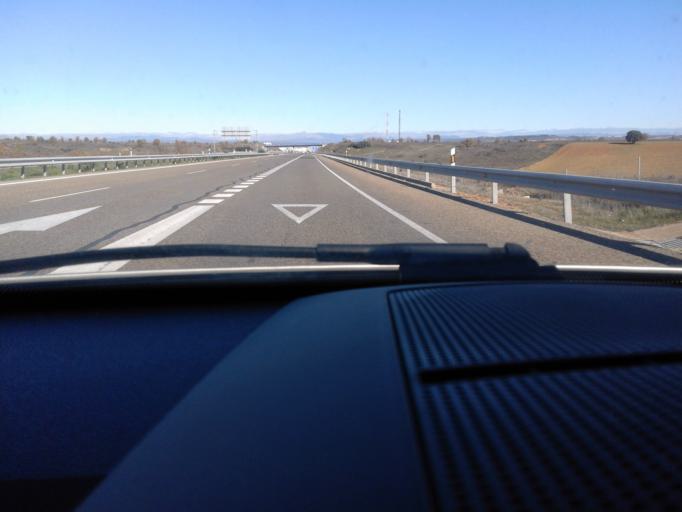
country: ES
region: Castille and Leon
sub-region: Provincia de Leon
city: Onzonilla
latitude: 42.5098
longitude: -5.5966
